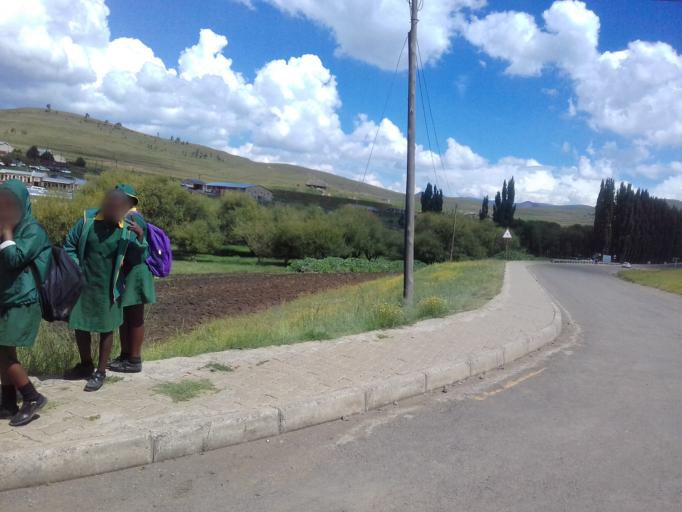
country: LS
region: Thaba-Tseka
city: Thaba-Tseka
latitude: -29.5207
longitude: 28.6038
